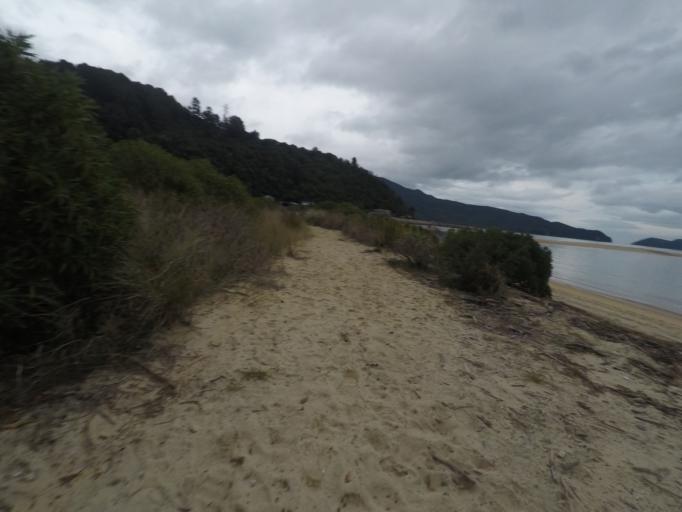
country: NZ
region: Tasman
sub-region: Tasman District
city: Motueka
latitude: -41.0115
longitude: 173.0073
